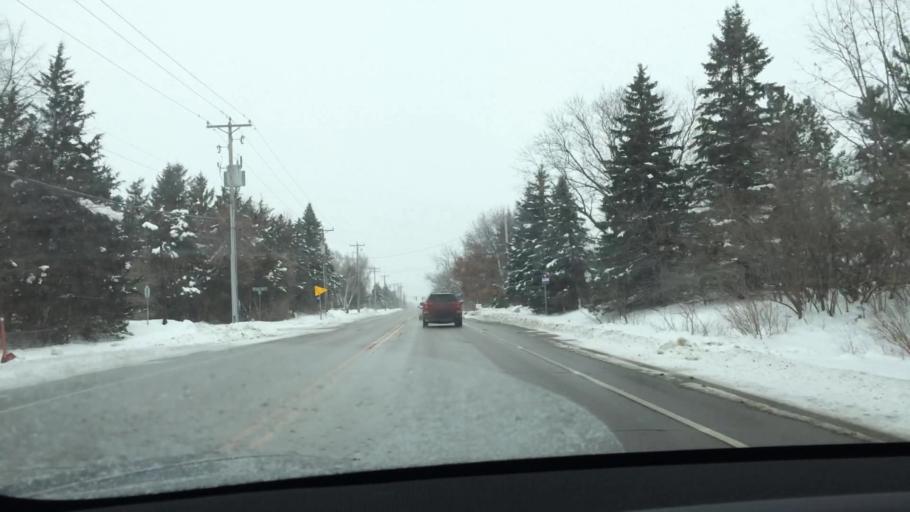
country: US
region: Minnesota
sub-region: Ramsey County
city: Shoreview
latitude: 45.1042
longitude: -93.1273
